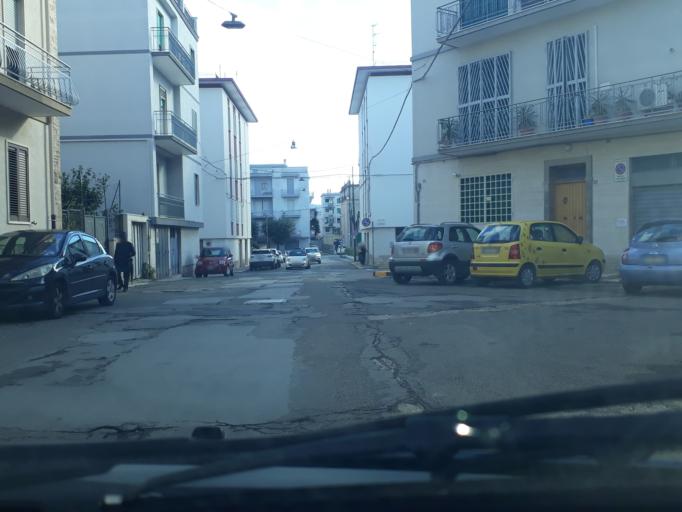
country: IT
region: Apulia
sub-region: Provincia di Brindisi
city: Fasano
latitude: 40.8327
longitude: 17.3551
